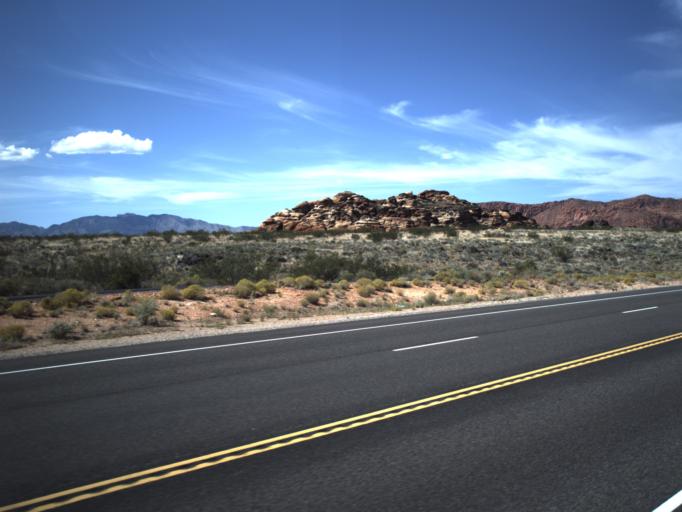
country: US
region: Utah
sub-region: Washington County
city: Santa Clara
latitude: 37.1659
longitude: -113.6132
